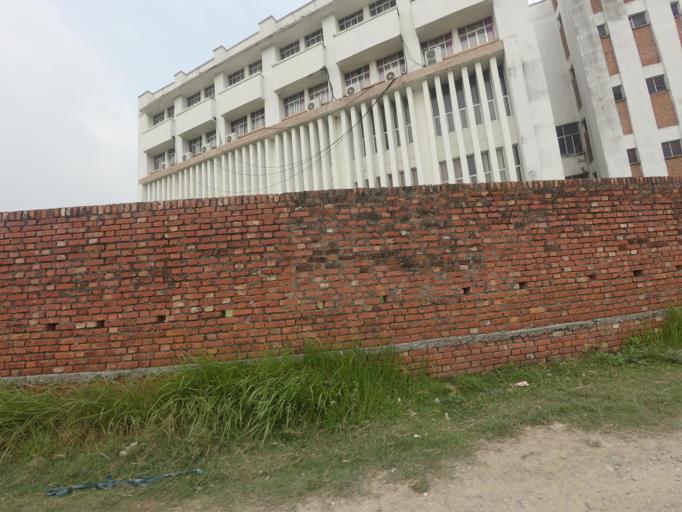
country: NP
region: Western Region
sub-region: Lumbini Zone
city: Bhairahawa
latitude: 27.4875
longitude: 83.4488
